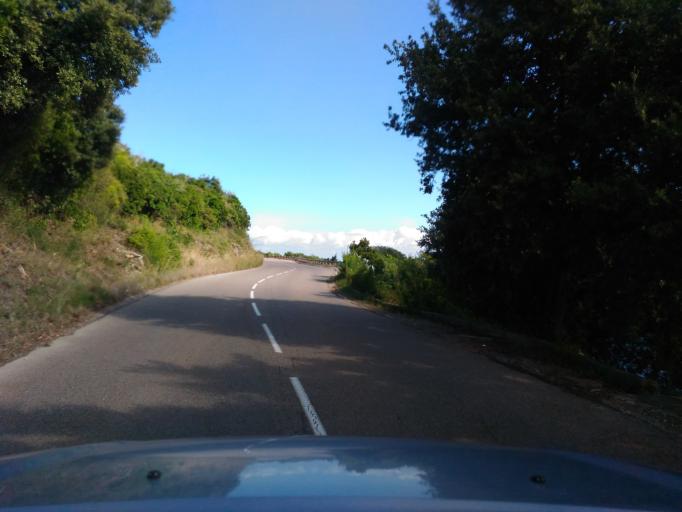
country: FR
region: Corsica
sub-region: Departement de la Haute-Corse
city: Brando
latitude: 42.7913
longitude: 9.4873
